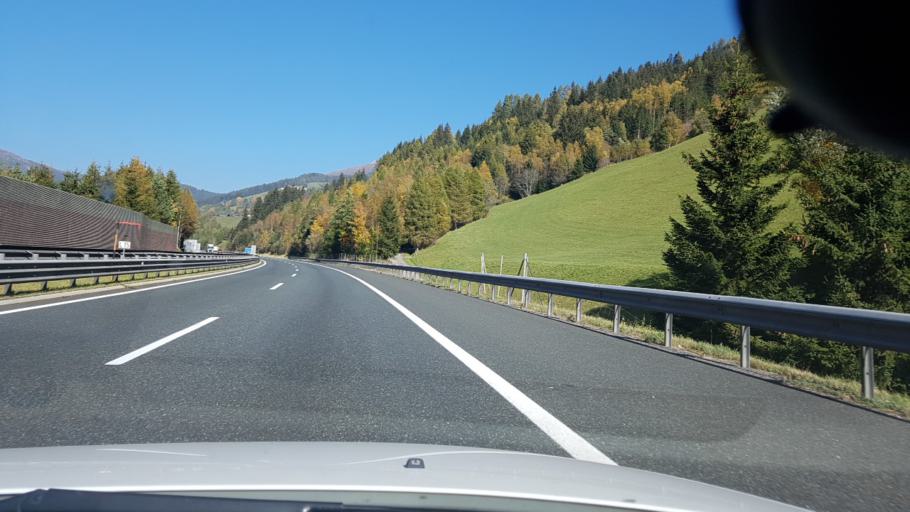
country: AT
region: Salzburg
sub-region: Politischer Bezirk Tamsweg
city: Sankt Michael im Lungau
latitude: 47.0007
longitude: 13.6206
